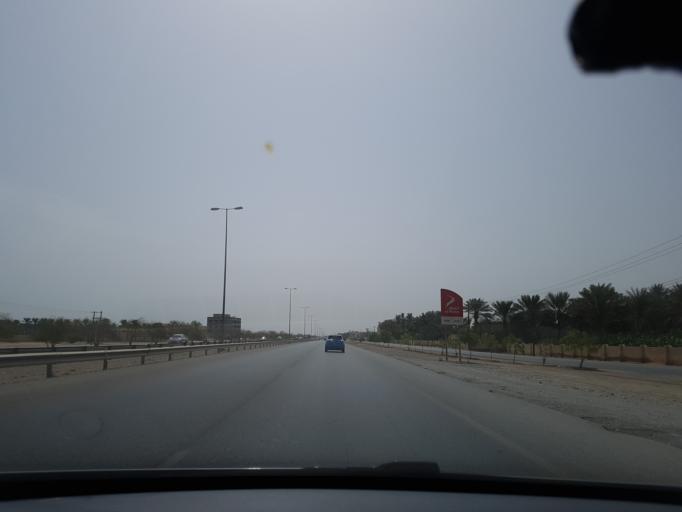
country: OM
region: Al Batinah
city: As Suwayq
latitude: 23.8338
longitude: 57.3934
